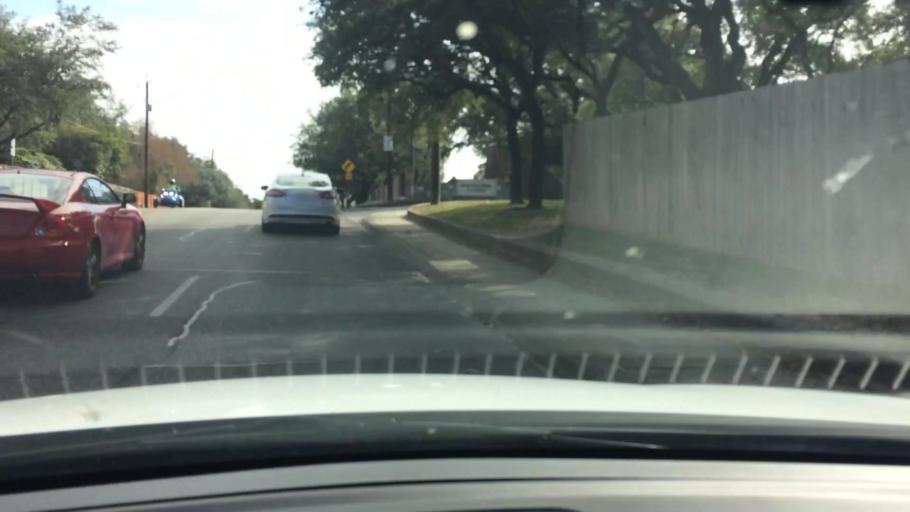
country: US
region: Texas
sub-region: Bexar County
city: Hollywood Park
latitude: 29.5755
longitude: -98.4674
